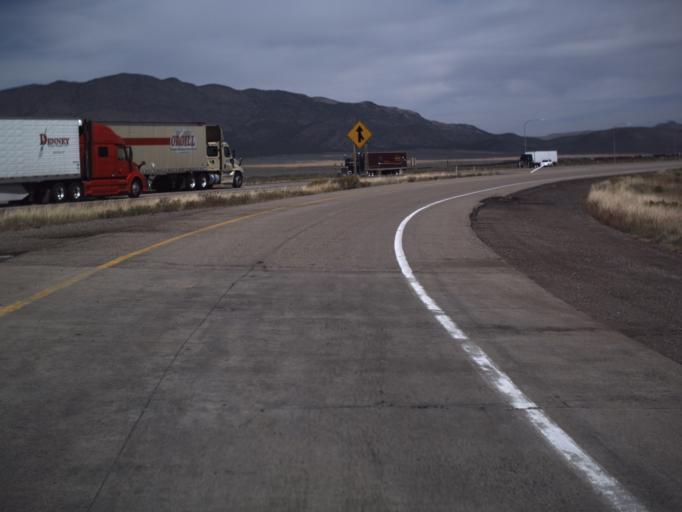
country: US
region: Utah
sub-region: Iron County
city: Parowan
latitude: 37.9827
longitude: -112.7360
